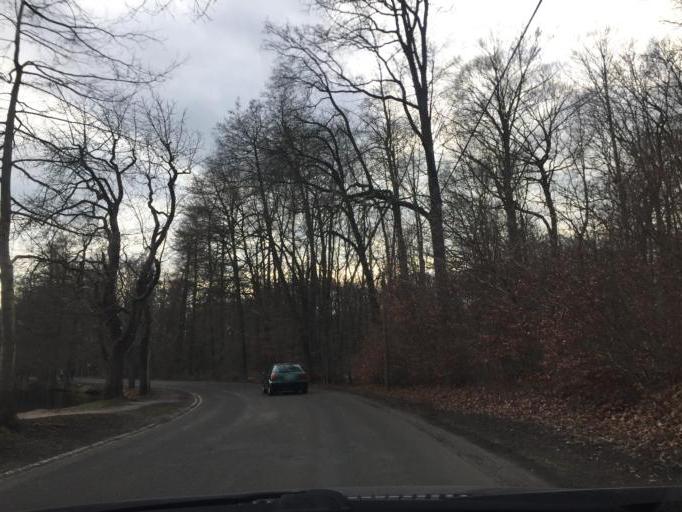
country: DE
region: Saxony
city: Moritzburg
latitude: 51.1691
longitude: 13.6728
